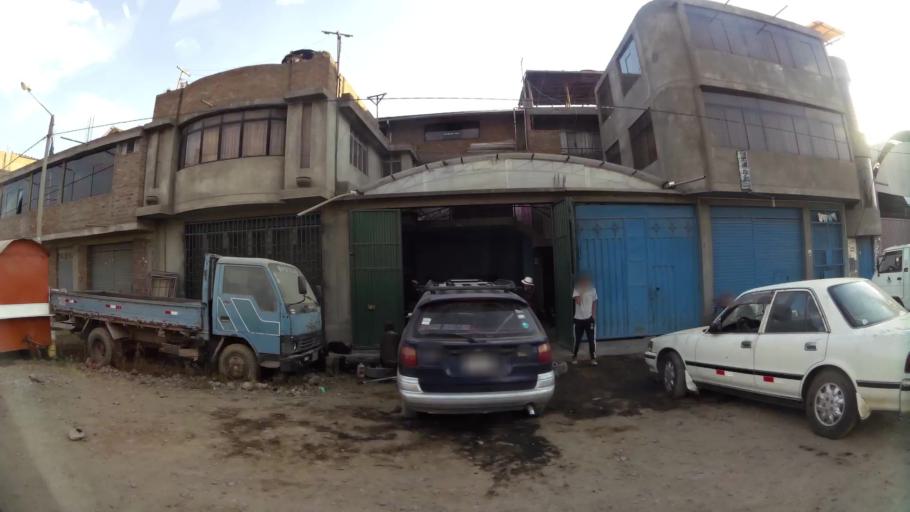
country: PE
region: Junin
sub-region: Provincia de Huancayo
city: Pilcomay
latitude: -12.0360
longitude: -75.2278
